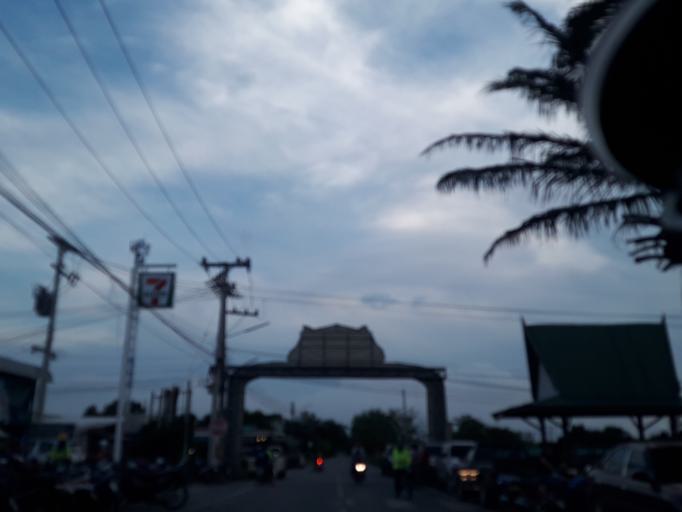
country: TH
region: Pathum Thani
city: Nong Suea
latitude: 14.1366
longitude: 100.8690
